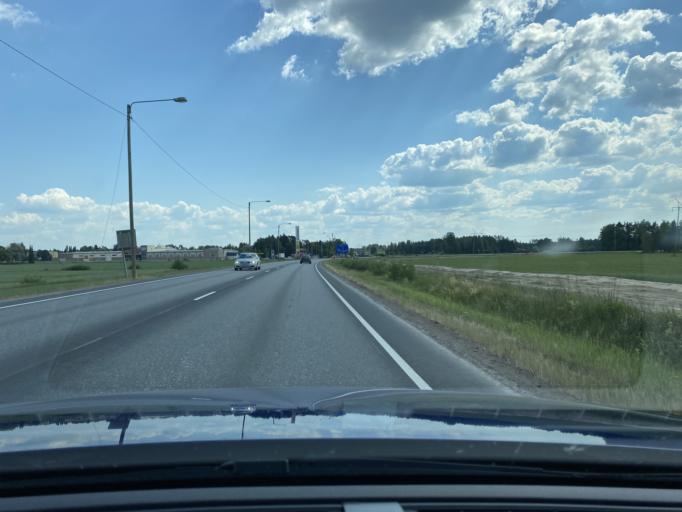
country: FI
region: Satakunta
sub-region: Rauma
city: Eura
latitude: 61.1343
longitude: 22.1223
